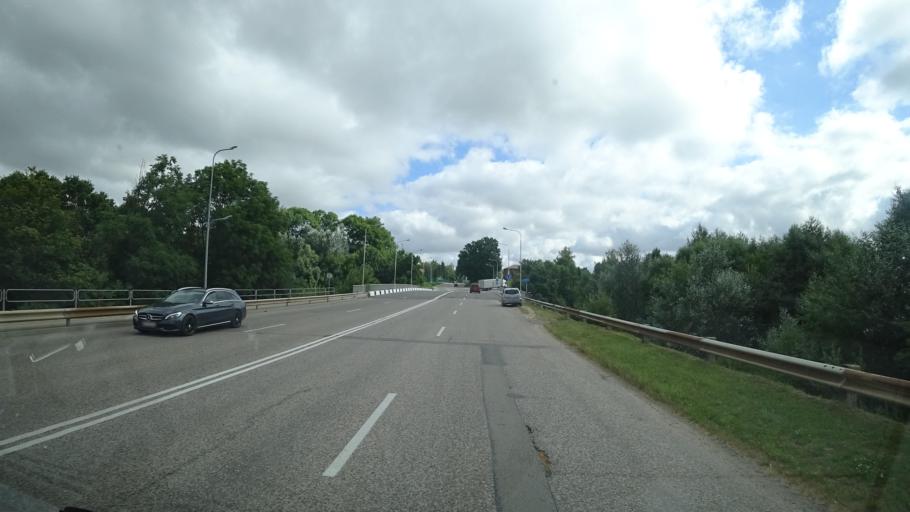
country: LT
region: Marijampoles apskritis
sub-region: Marijampole Municipality
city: Marijampole
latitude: 54.5363
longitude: 23.3382
